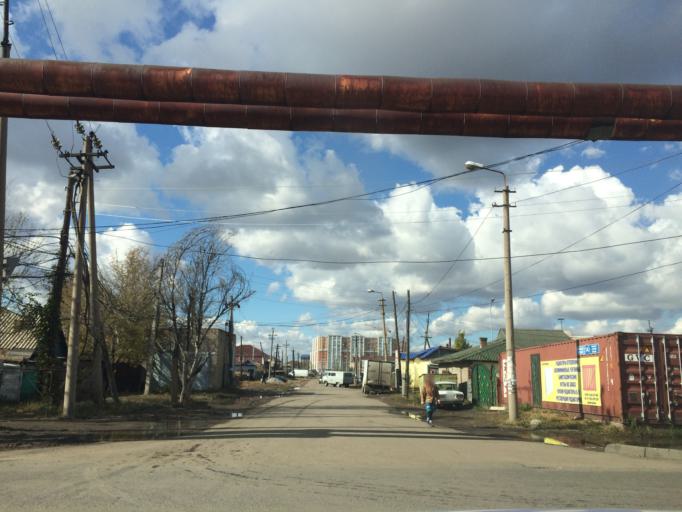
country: KZ
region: Astana Qalasy
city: Astana
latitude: 51.1909
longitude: 71.3942
